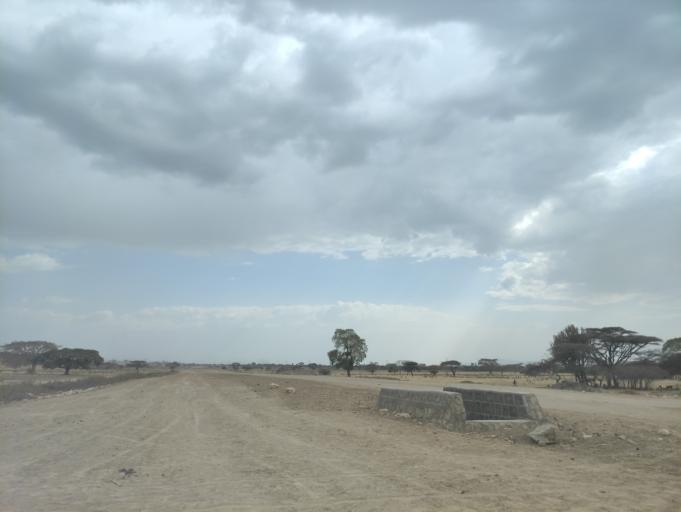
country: ET
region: Oromiya
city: Shashemene
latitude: 7.4297
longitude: 38.6675
